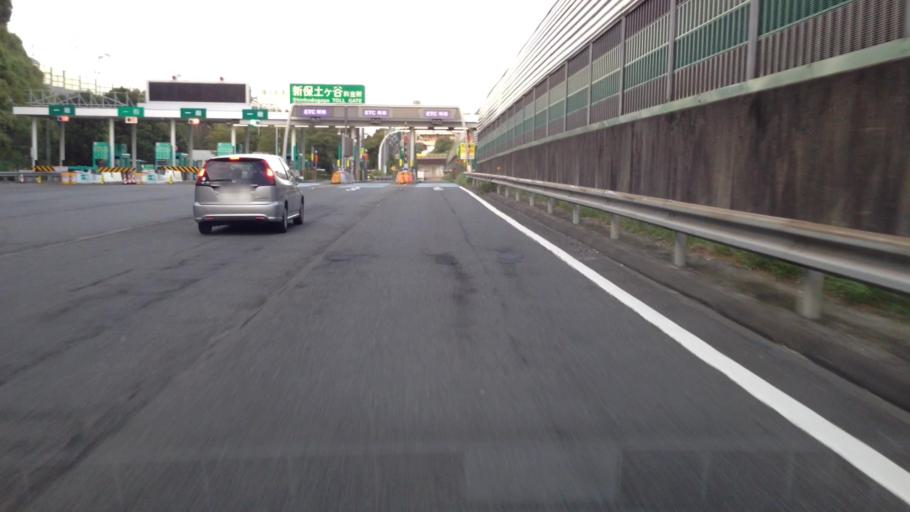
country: JP
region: Kanagawa
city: Yokohama
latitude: 35.4522
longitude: 139.5747
